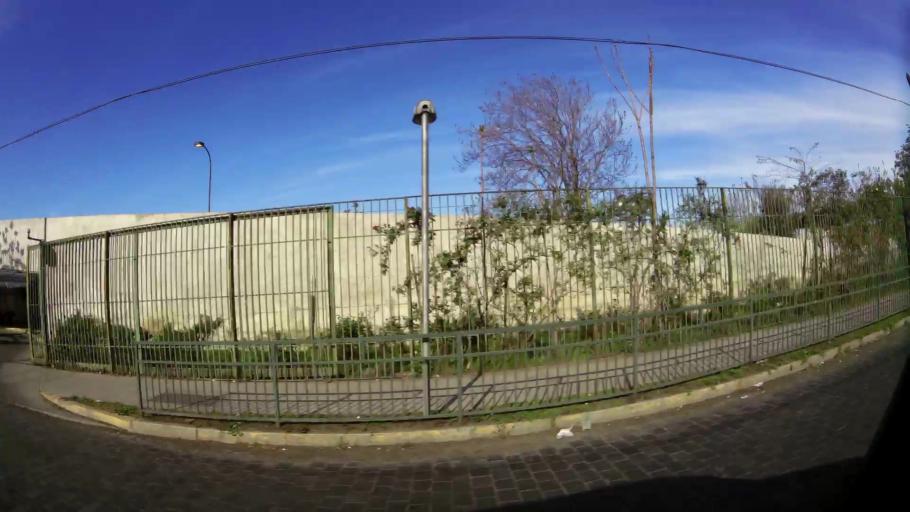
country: CL
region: Santiago Metropolitan
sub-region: Provincia de Santiago
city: Santiago
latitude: -33.4562
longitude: -70.6805
